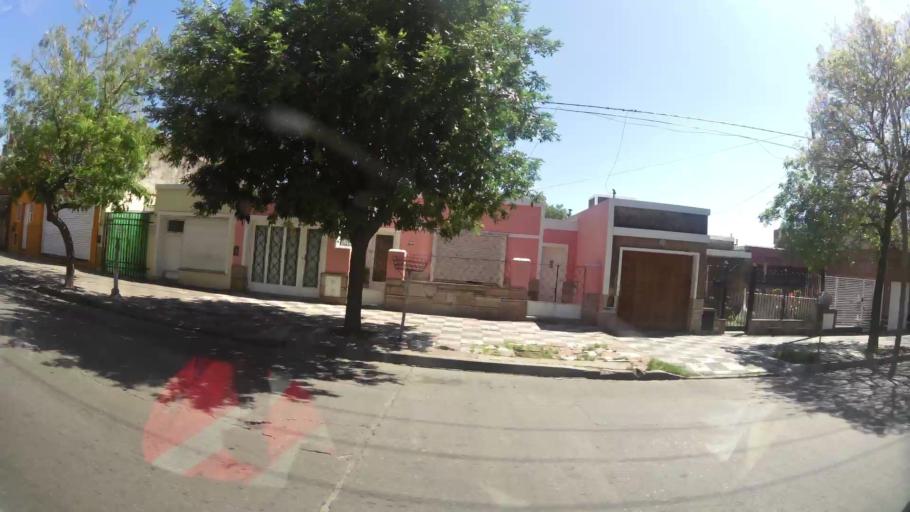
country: AR
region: Cordoba
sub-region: Departamento de Capital
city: Cordoba
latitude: -31.4210
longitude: -64.2094
